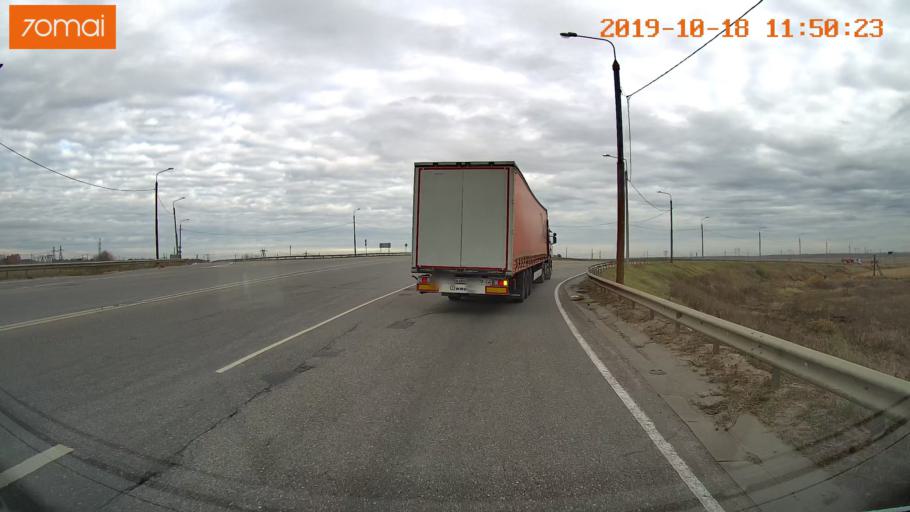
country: RU
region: Rjazan
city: Mikhaylov
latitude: 54.2603
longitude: 39.0026
